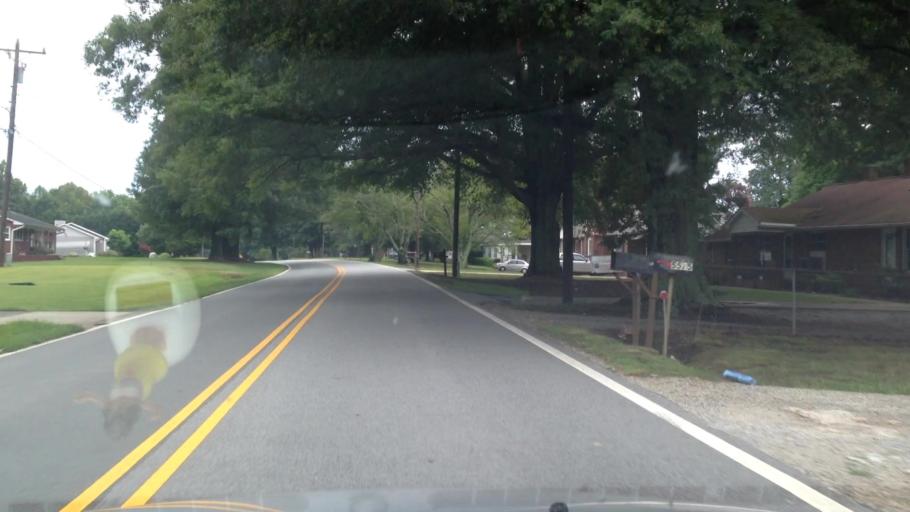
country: US
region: North Carolina
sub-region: Forsyth County
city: Walkertown
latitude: 36.1551
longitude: -80.1253
